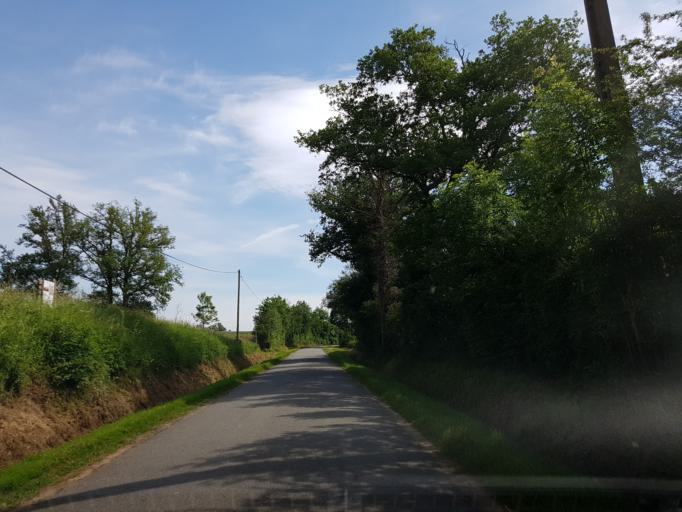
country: FR
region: Poitou-Charentes
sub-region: Departement de la Charente
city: Etagnac
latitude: 45.9362
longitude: 0.7426
